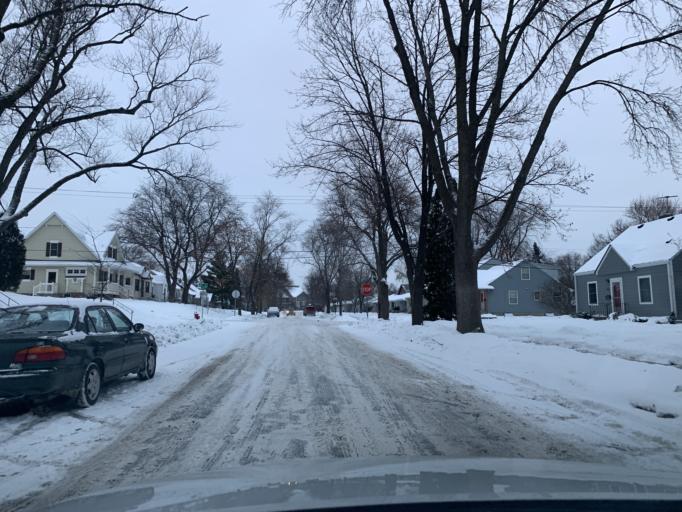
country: US
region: Minnesota
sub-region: Hennepin County
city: Saint Louis Park
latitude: 44.9268
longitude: -93.3470
